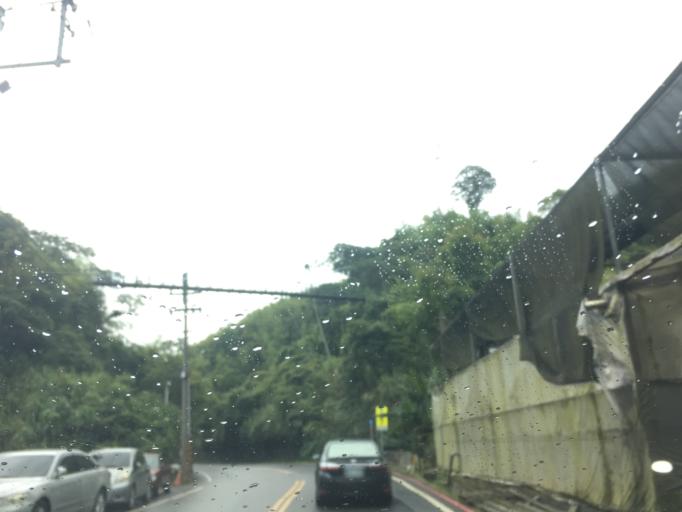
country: TW
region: Taiwan
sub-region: Yunlin
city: Douliu
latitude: 23.5598
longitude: 120.6047
